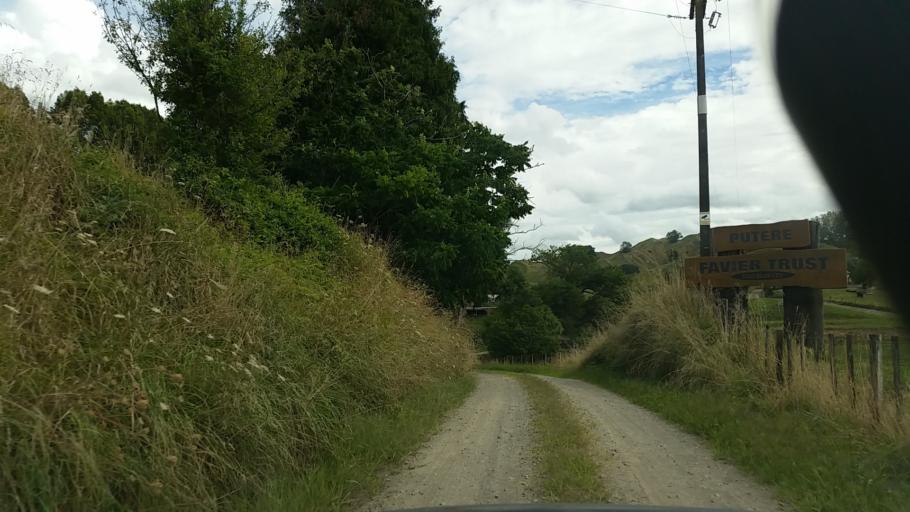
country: NZ
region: Taranaki
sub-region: South Taranaki District
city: Eltham
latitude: -39.2572
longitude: 174.5629
